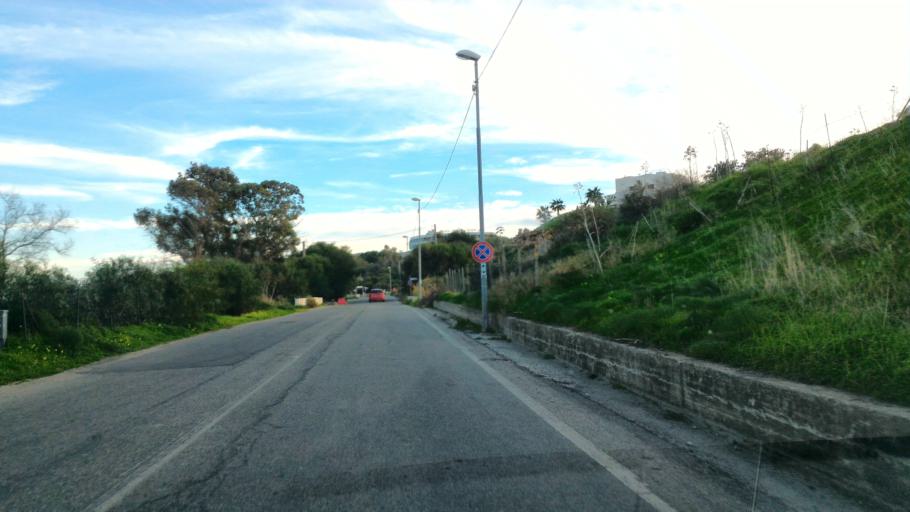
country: IT
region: Calabria
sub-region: Provincia di Crotone
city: Crotone
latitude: 39.0530
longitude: 17.1391
